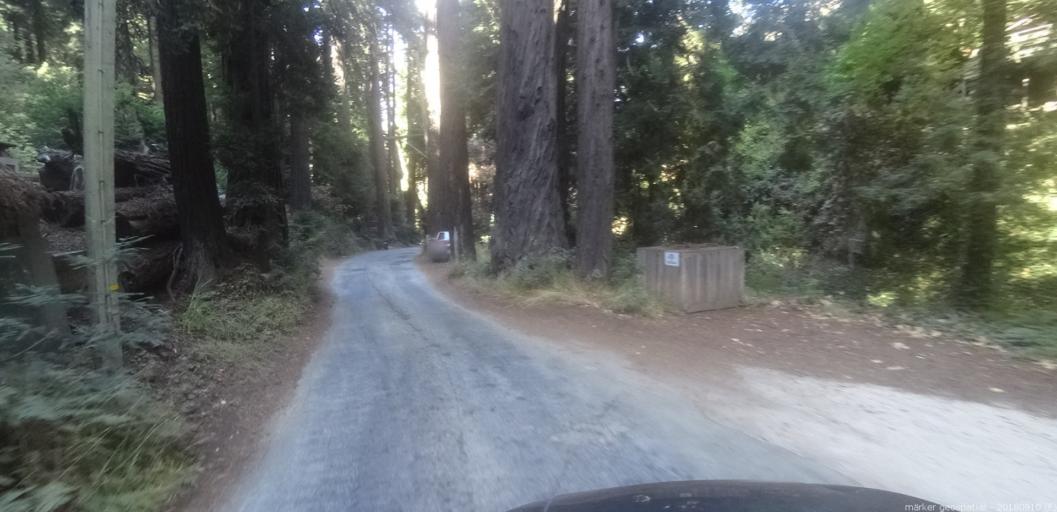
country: US
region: California
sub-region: Monterey County
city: Carmel-by-the-Sea
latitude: 36.4010
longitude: -121.8997
